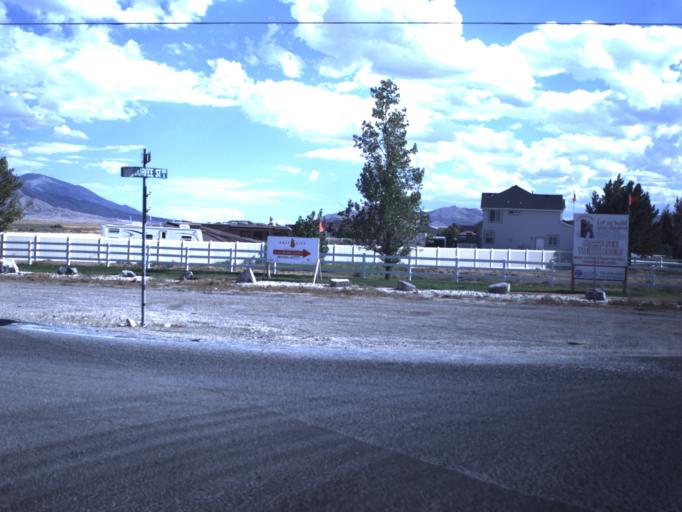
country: US
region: Utah
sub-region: Tooele County
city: Grantsville
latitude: 40.5924
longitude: -112.4235
